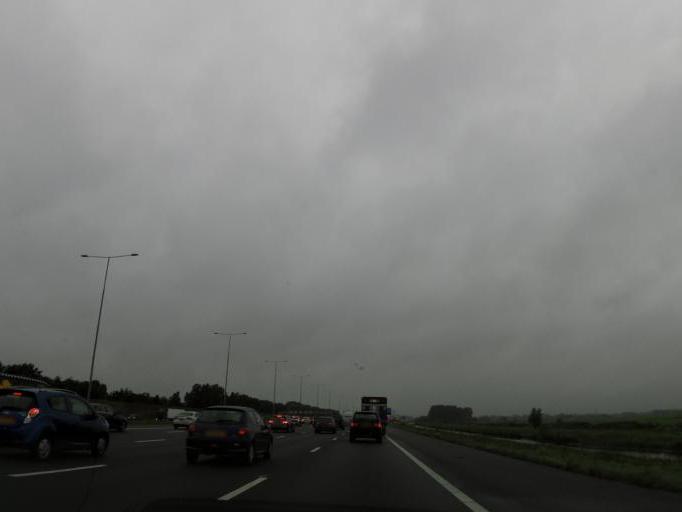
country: NL
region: Utrecht
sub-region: Stichtse Vecht
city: Vreeland
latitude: 52.2452
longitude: 4.9719
